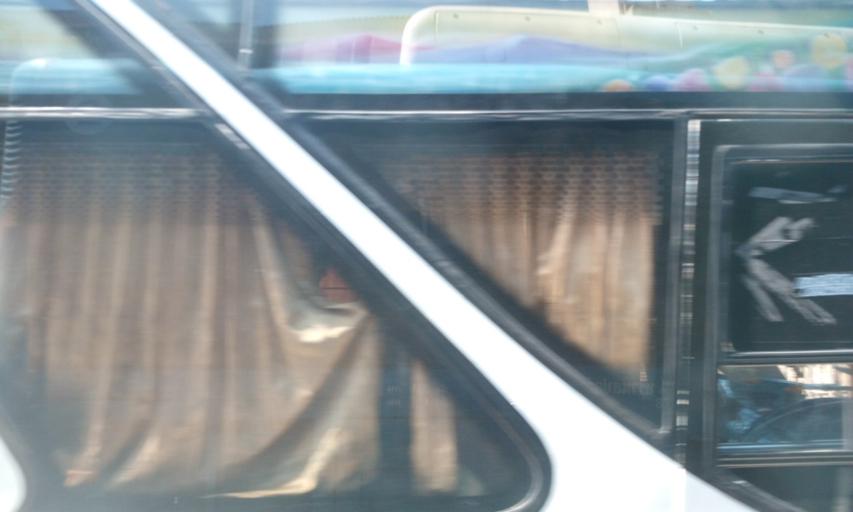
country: TH
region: Samut Prakan
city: Bang Bo District
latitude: 13.5558
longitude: 100.7718
